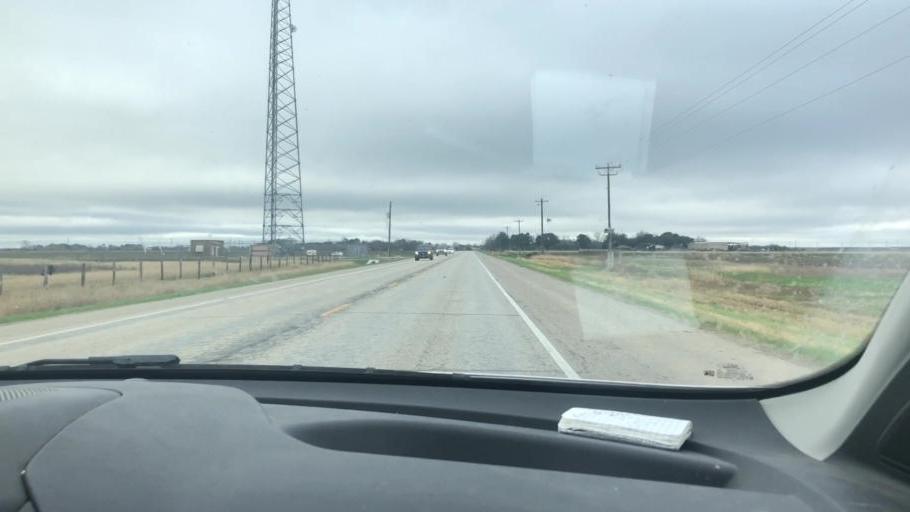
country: US
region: Texas
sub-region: Wharton County
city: Boling
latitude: 29.2331
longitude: -96.0375
